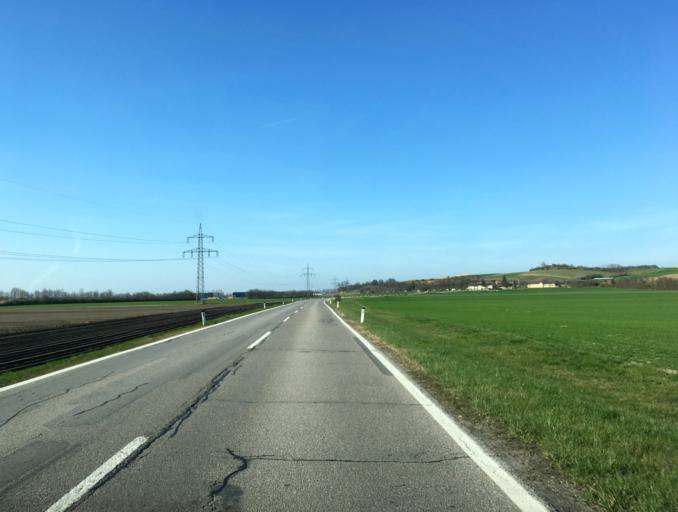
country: AT
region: Lower Austria
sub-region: Politischer Bezirk Bruck an der Leitha
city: Enzersdorf an der Fischa
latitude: 48.0540
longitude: 16.6172
